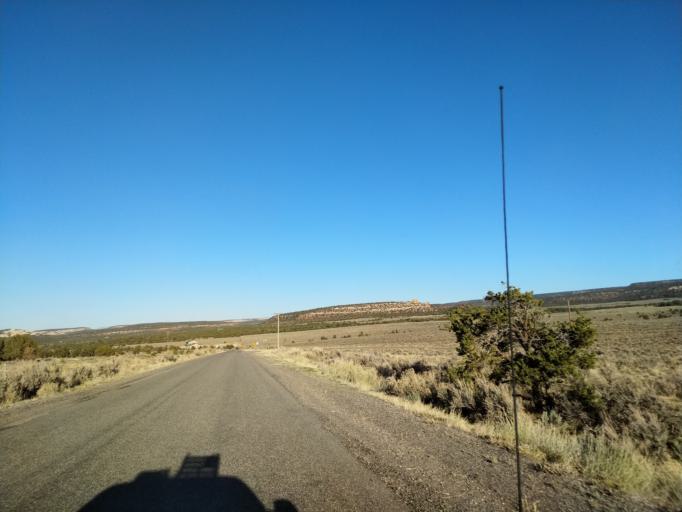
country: US
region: Colorado
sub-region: Mesa County
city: Loma
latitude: 38.9522
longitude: -108.9448
